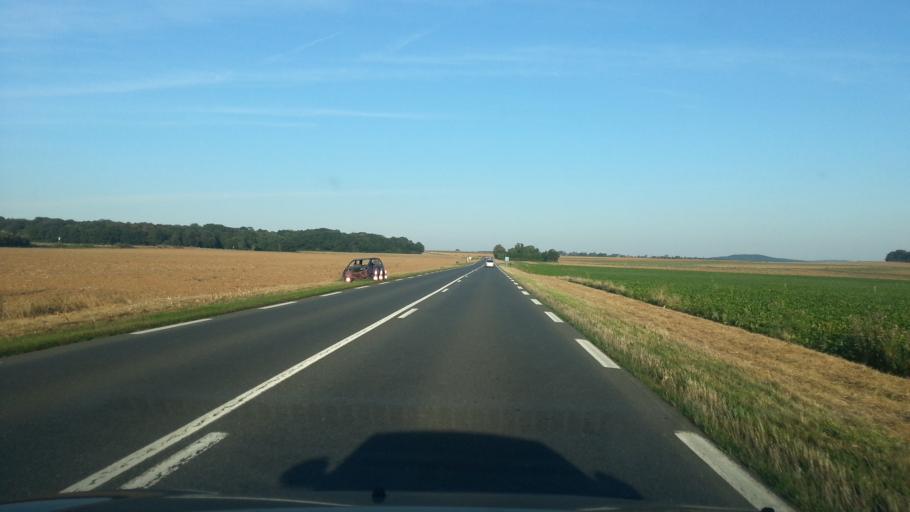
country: FR
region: Picardie
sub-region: Departement de l'Oise
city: Sacy-le-Grand
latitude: 49.3765
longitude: 2.5366
